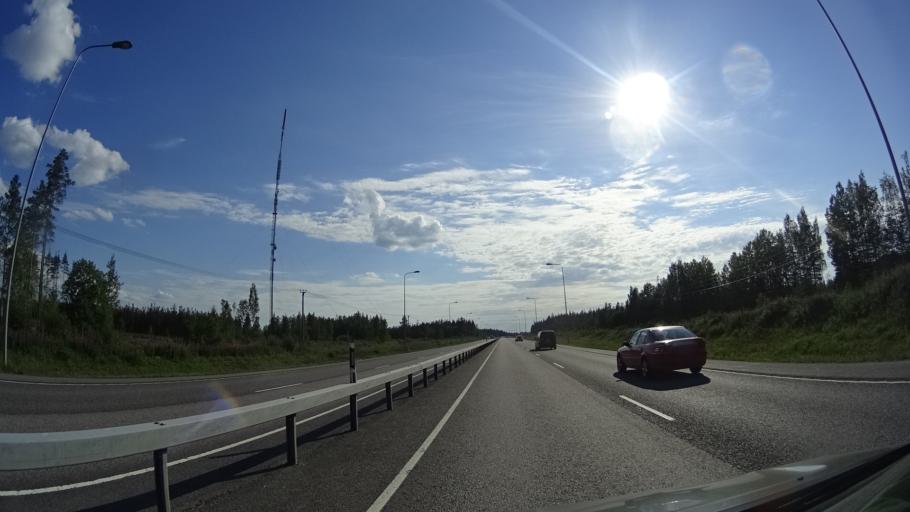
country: FI
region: South Karelia
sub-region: Lappeenranta
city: Joutseno
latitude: 61.1344
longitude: 28.5454
